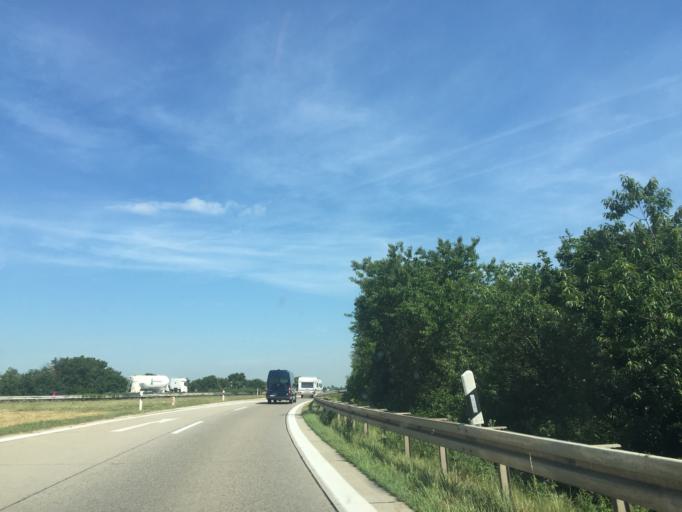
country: DE
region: Baden-Wuerttemberg
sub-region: Karlsruhe Region
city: Eppelheim
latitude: 49.4200
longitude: 8.6346
